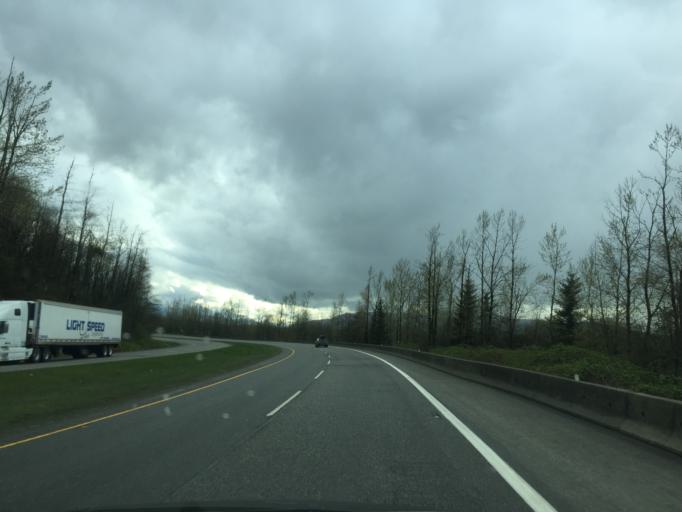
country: CA
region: British Columbia
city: Agassiz
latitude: 49.2913
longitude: -121.6661
